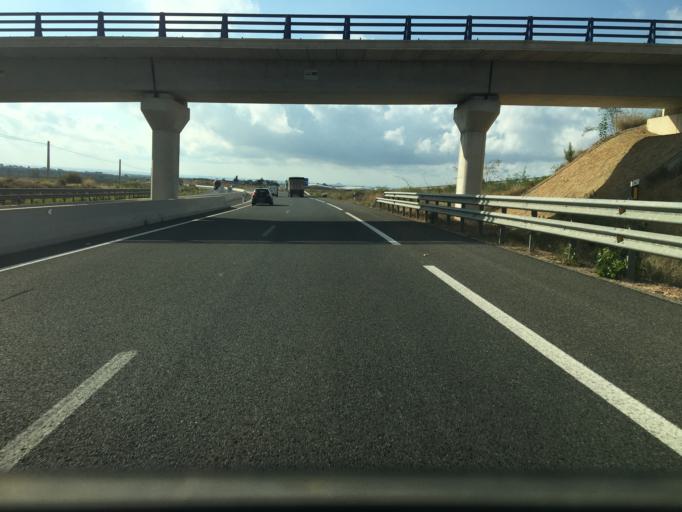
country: ES
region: Murcia
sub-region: Murcia
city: San Javier
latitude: 37.8675
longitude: -0.9055
